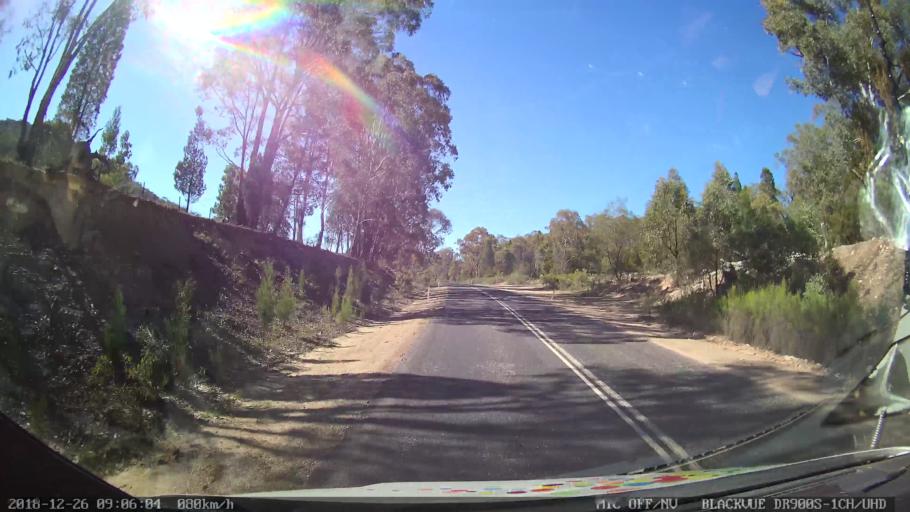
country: AU
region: New South Wales
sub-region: Mid-Western Regional
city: Kandos
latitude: -32.6897
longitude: 150.0045
